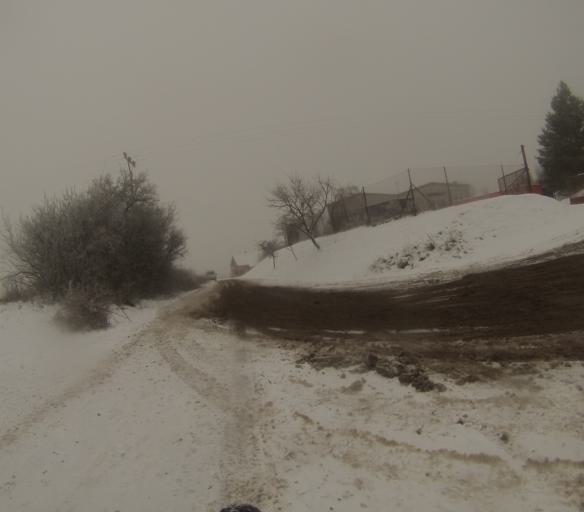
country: CZ
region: South Moravian
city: Strelice
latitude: 49.1492
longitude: 16.4972
